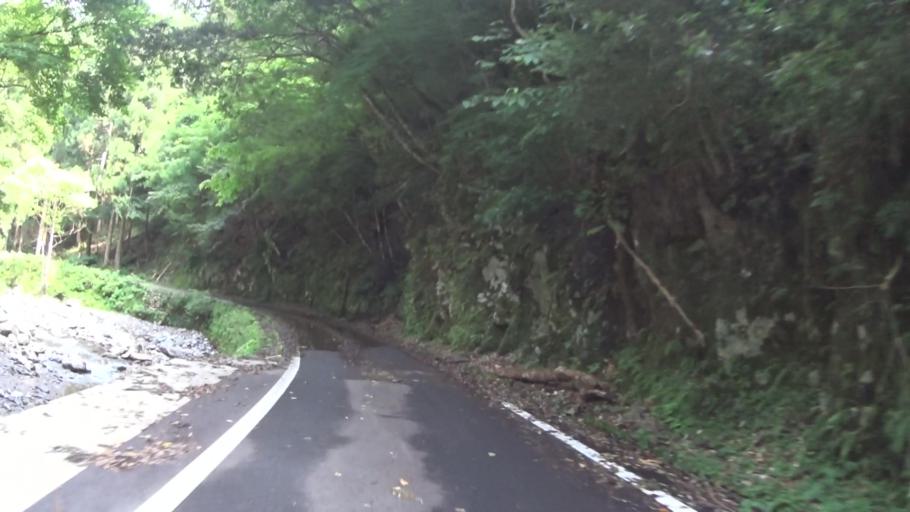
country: JP
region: Fukui
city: Obama
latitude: 35.2901
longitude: 135.6441
